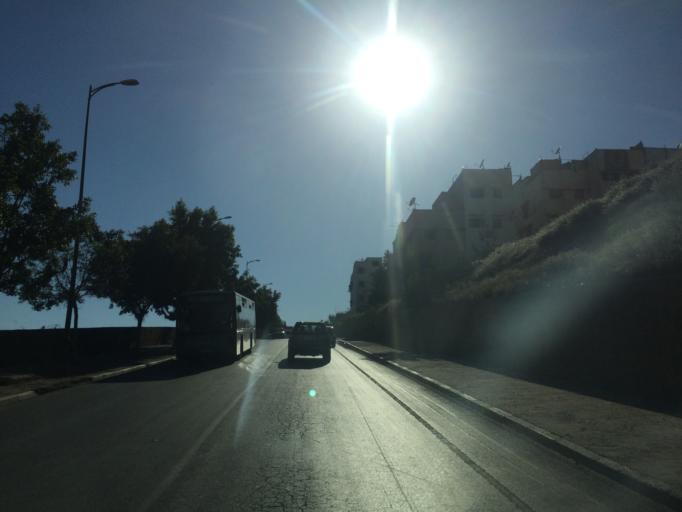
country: MA
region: Rabat-Sale-Zemmour-Zaer
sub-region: Rabat
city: Rabat
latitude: 33.9911
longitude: -6.8109
